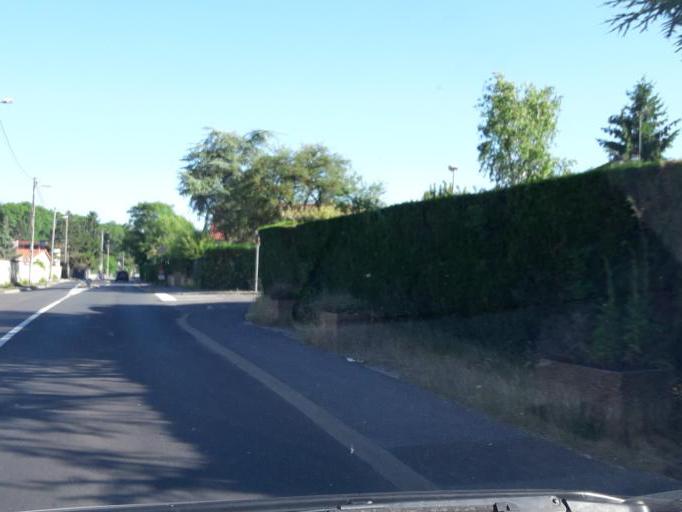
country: FR
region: Ile-de-France
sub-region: Departement de l'Essonne
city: Itteville
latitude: 48.5293
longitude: 2.3411
